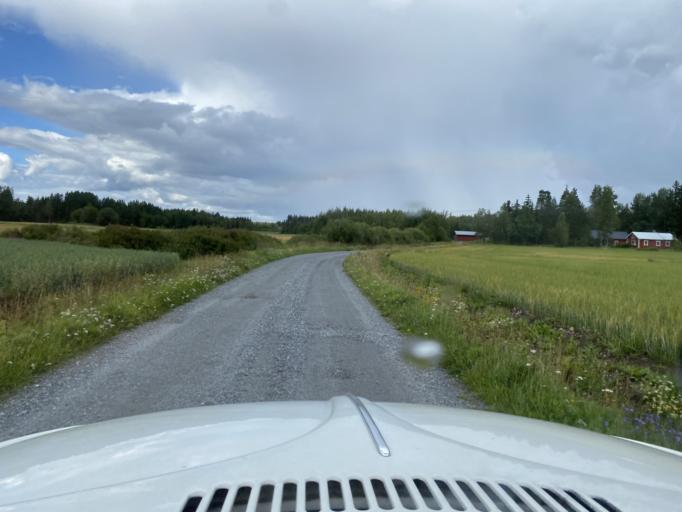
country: FI
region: Pirkanmaa
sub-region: Lounais-Pirkanmaa
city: Punkalaidun
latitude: 61.1230
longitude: 23.0594
